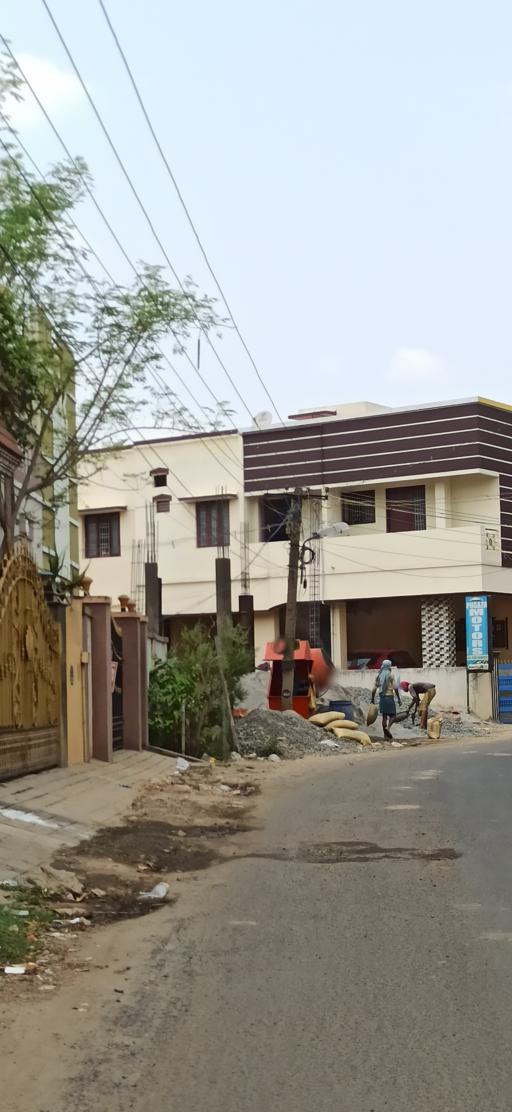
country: IN
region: Tamil Nadu
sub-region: Thiruvallur
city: Porur
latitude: 13.0182
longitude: 80.1444
